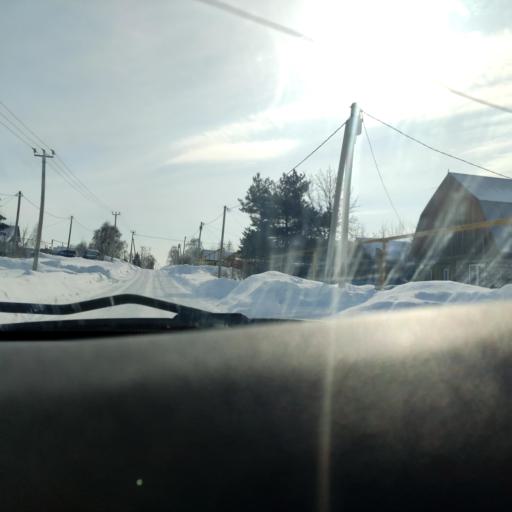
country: RU
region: Samara
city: Rozhdestveno
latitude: 53.2454
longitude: 50.0633
